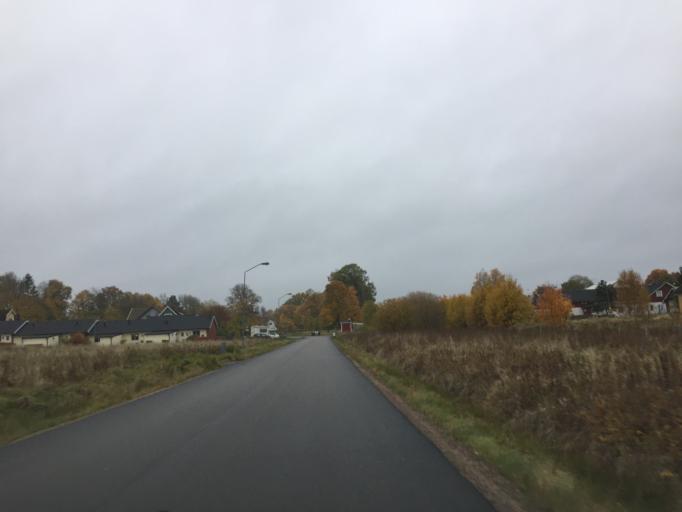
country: SE
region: Vaestra Goetaland
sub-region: Trollhattan
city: Sjuntorp
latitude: 58.1582
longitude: 12.3079
